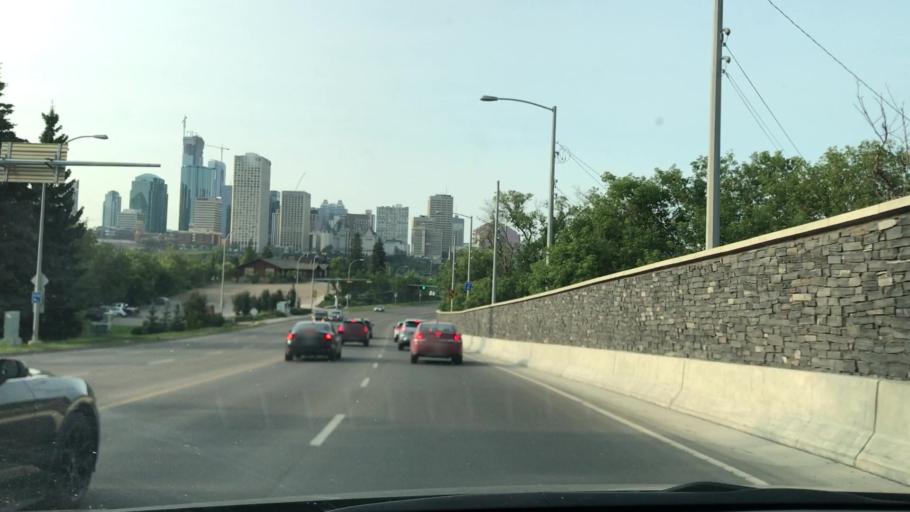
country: CA
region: Alberta
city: Edmonton
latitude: 53.5296
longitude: -113.4851
